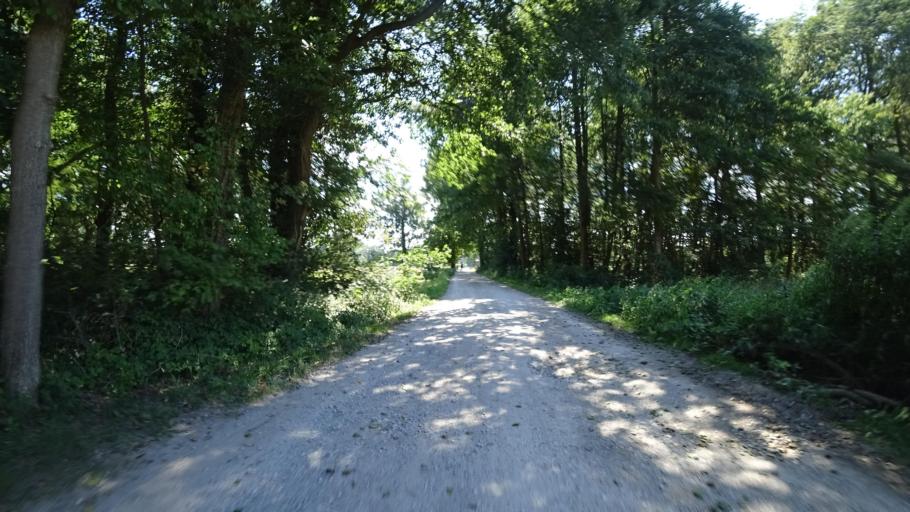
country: DE
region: North Rhine-Westphalia
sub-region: Regierungsbezirk Detmold
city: Guetersloh
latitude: 51.9335
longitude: 8.3980
